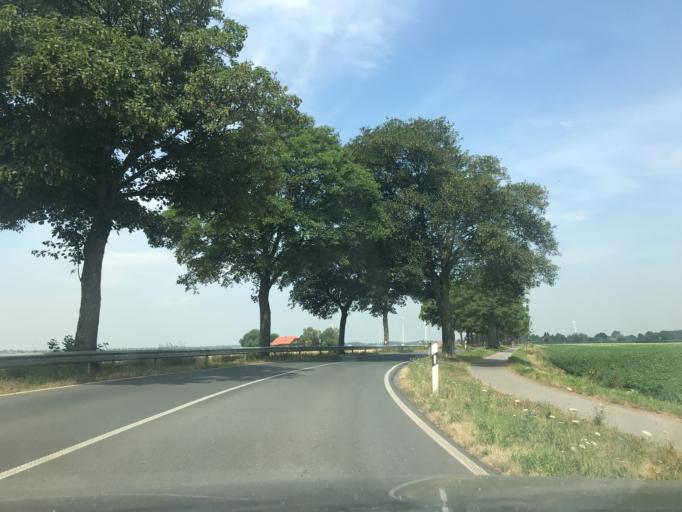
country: DE
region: North Rhine-Westphalia
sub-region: Regierungsbezirk Dusseldorf
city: Rheurdt
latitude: 51.4454
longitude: 6.4193
